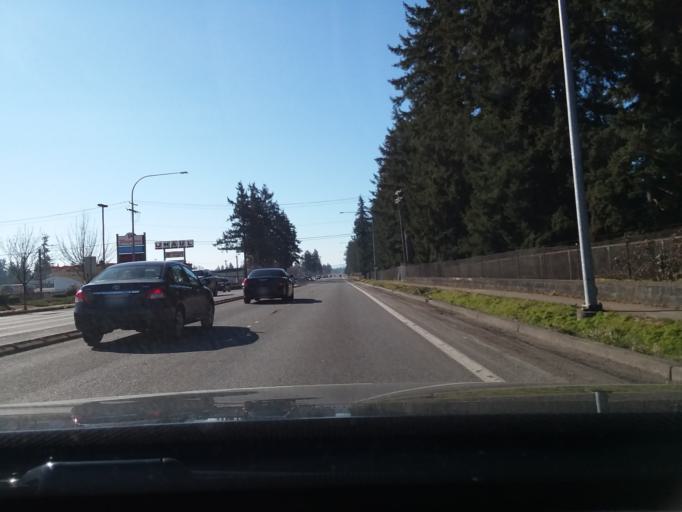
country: US
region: Washington
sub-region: Pierce County
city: Spanaway
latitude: 47.1186
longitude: -122.4350
